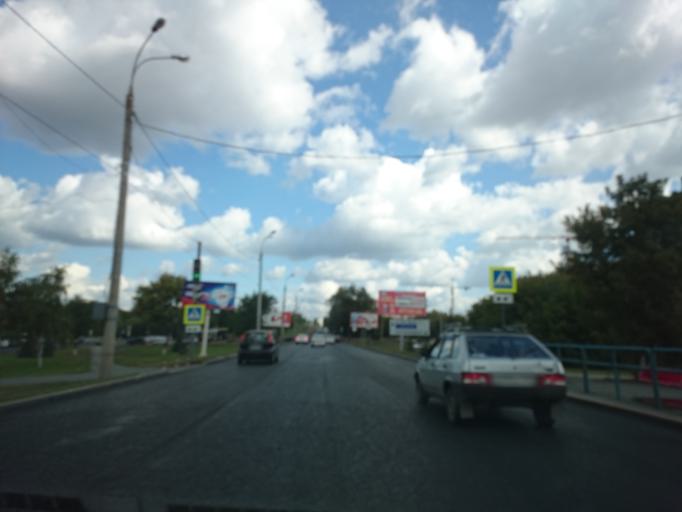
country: RU
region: Samara
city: Samara
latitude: 53.2239
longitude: 50.1703
